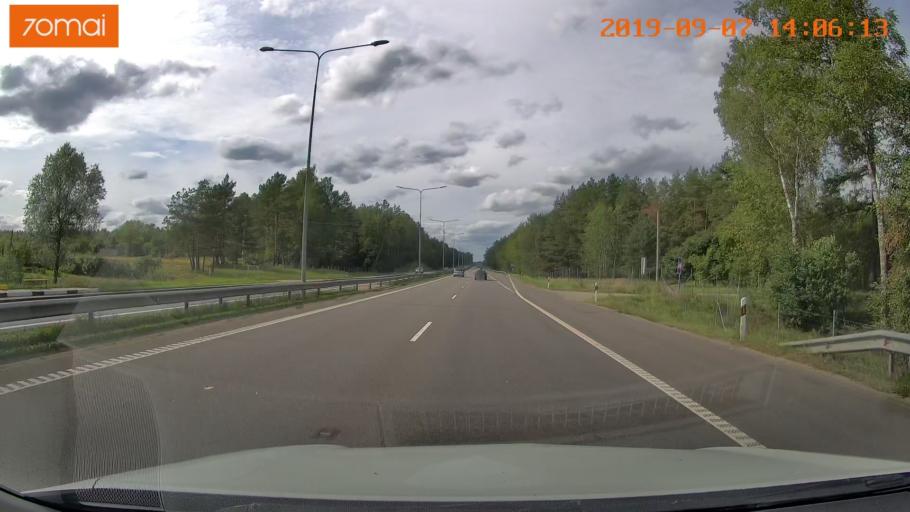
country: LT
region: Vilnius County
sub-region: Vilniaus Rajonas
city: Vievis
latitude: 54.7574
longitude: 24.8895
